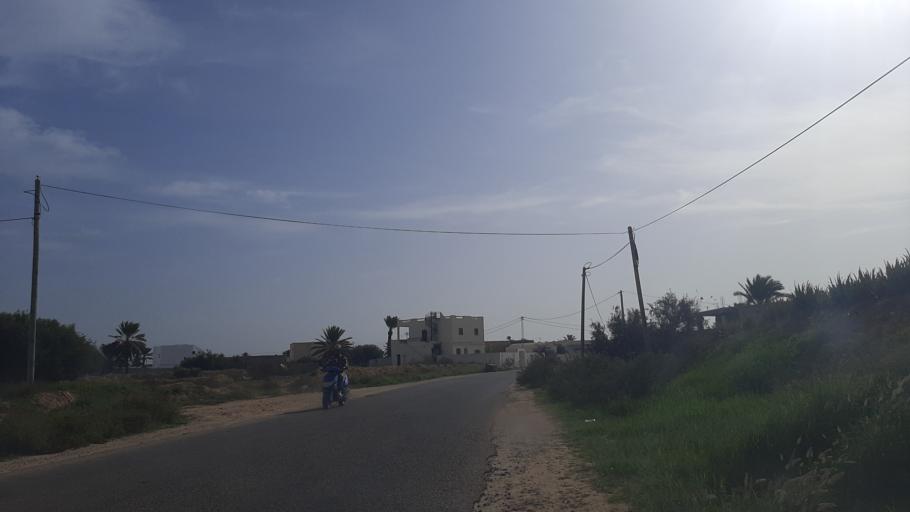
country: TN
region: Madanin
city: Midoun
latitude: 33.7955
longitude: 11.0295
